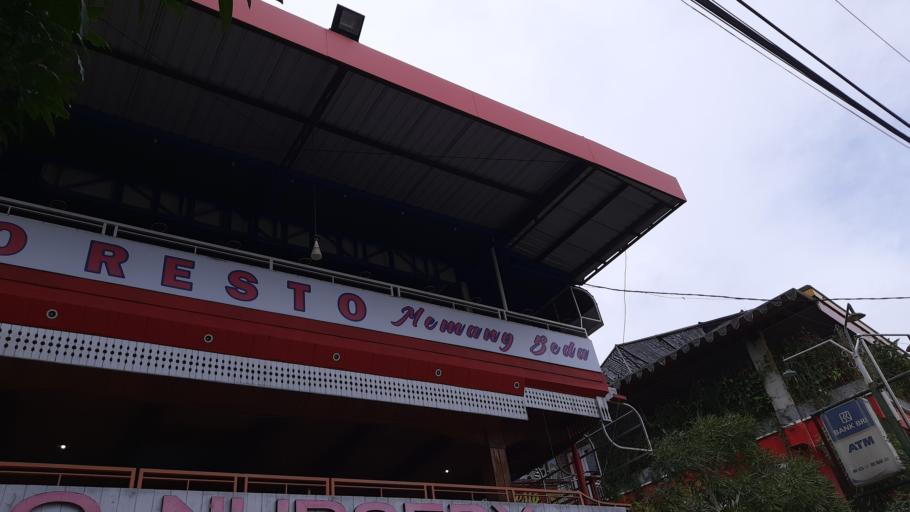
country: ID
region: North Kalimantan
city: Tanjung Palas
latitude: 2.1573
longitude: 117.4982
